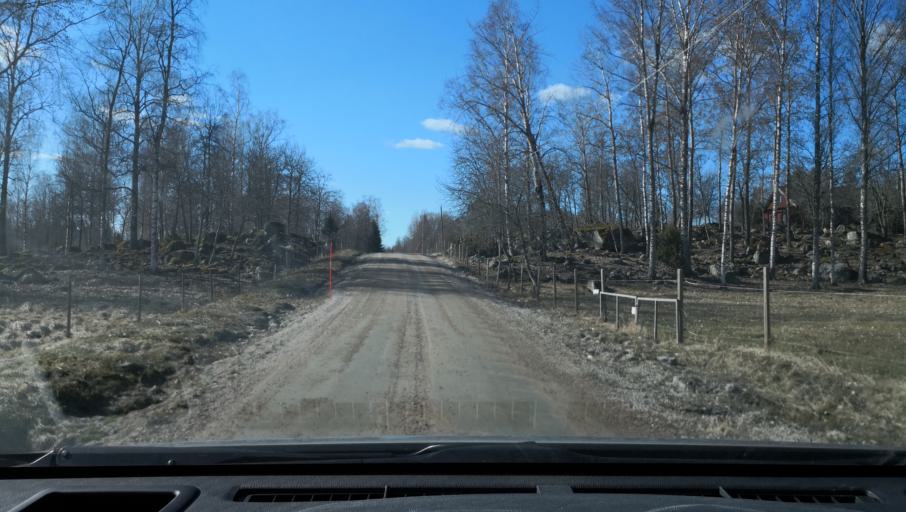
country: SE
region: Vaestmanland
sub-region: Sala Kommun
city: Sala
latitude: 60.1123
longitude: 16.6869
